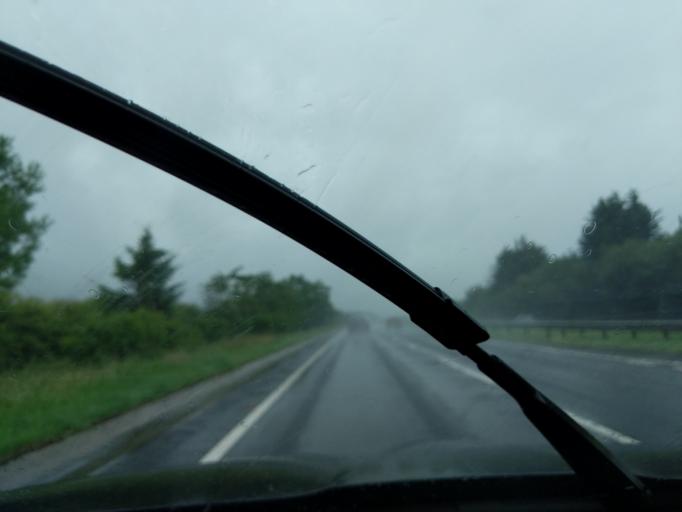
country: GB
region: England
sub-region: Northumberland
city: Alnwick
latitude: 55.3841
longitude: -1.7150
